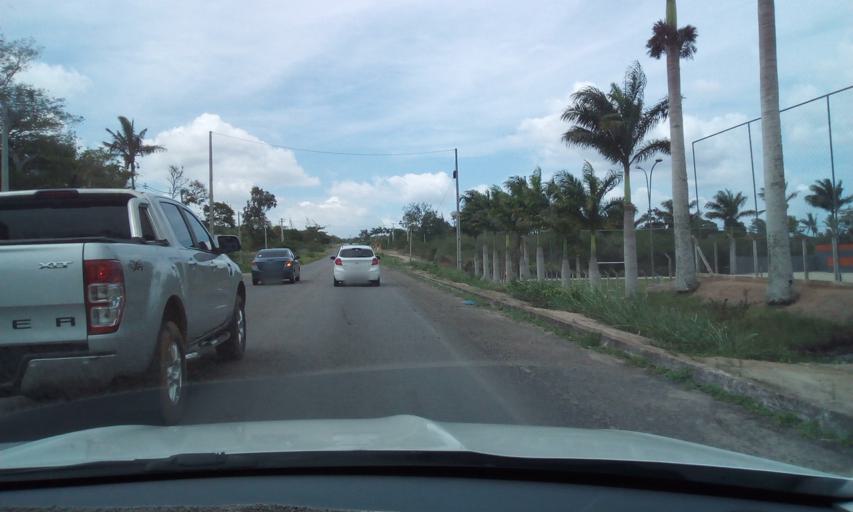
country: BR
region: Pernambuco
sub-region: Bezerros
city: Bezerros
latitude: -8.2820
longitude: -35.7423
